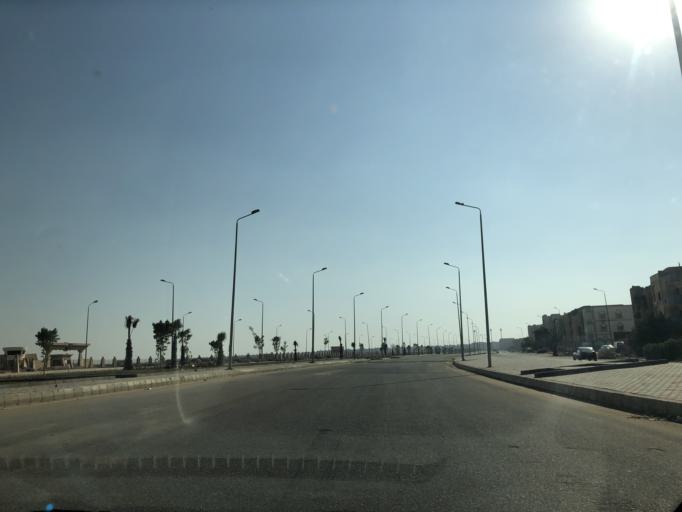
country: EG
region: Al Jizah
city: Madinat Sittah Uktubar
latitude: 29.9286
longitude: 31.0684
